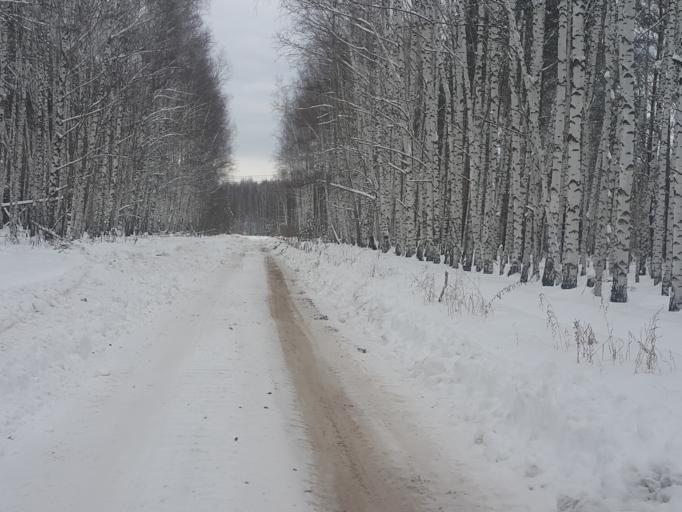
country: RU
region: Tambov
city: Platonovka
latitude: 52.8885
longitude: 41.8538
